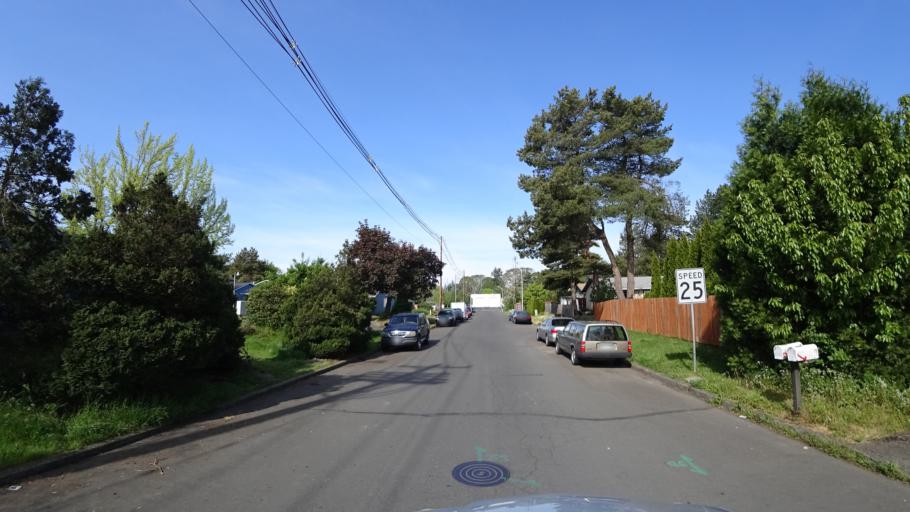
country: US
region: Oregon
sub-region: Washington County
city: Hillsboro
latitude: 45.5238
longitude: -122.9549
